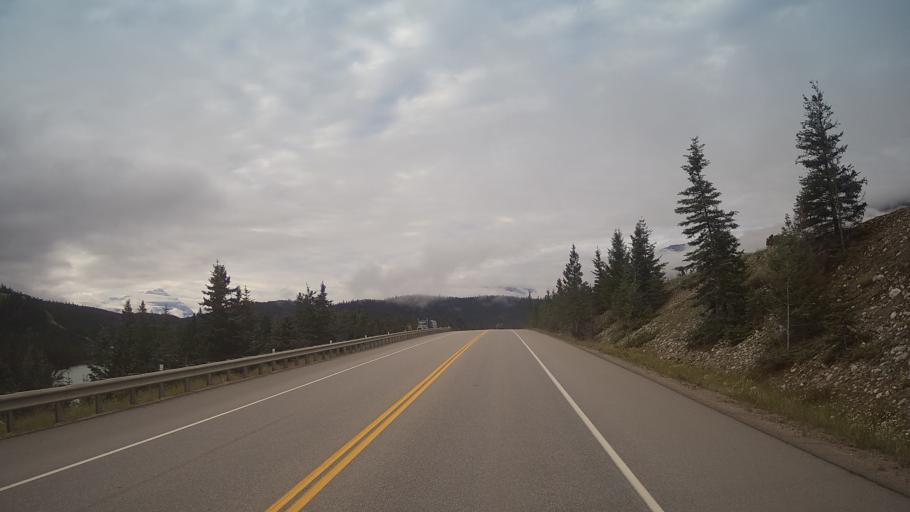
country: CA
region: Alberta
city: Jasper Park Lodge
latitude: 52.8786
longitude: -118.0729
